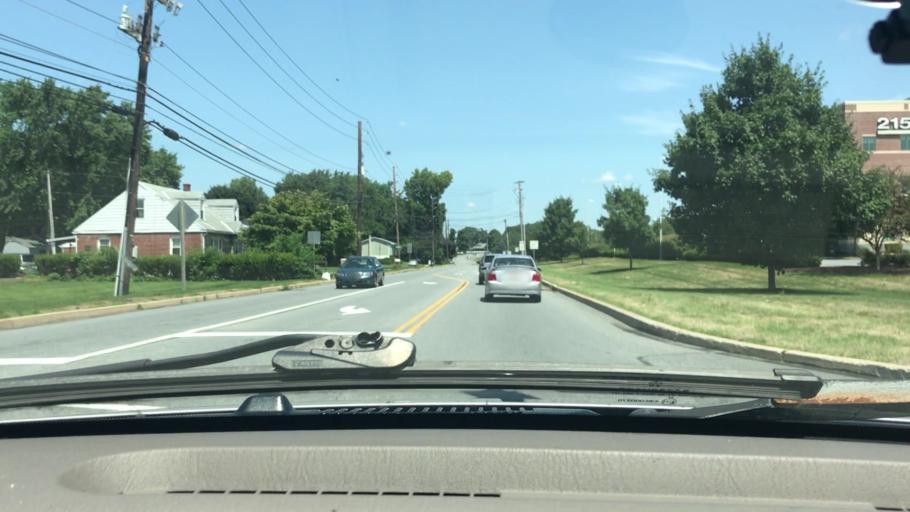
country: US
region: Pennsylvania
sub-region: Lancaster County
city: East Petersburg
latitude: 40.0636
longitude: -76.3589
